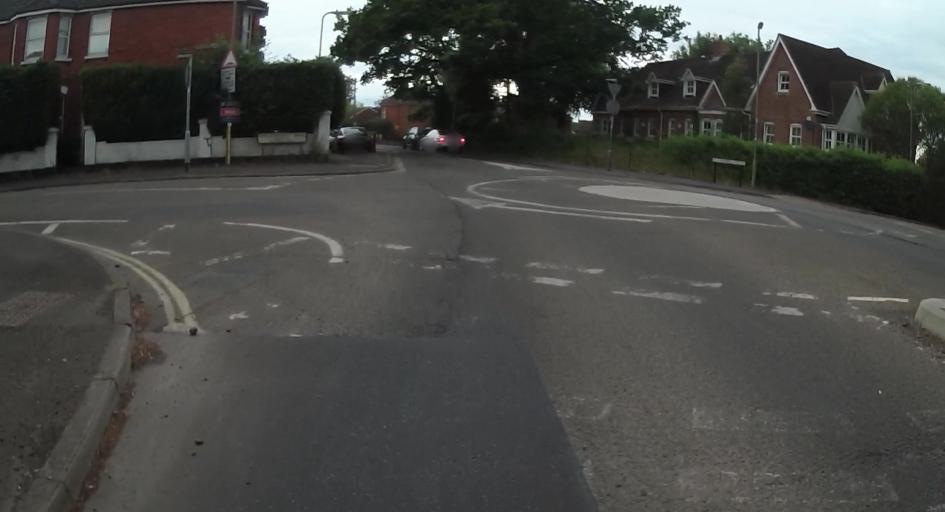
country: GB
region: England
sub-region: Hampshire
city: Aldershot
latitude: 51.2424
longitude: -0.7590
